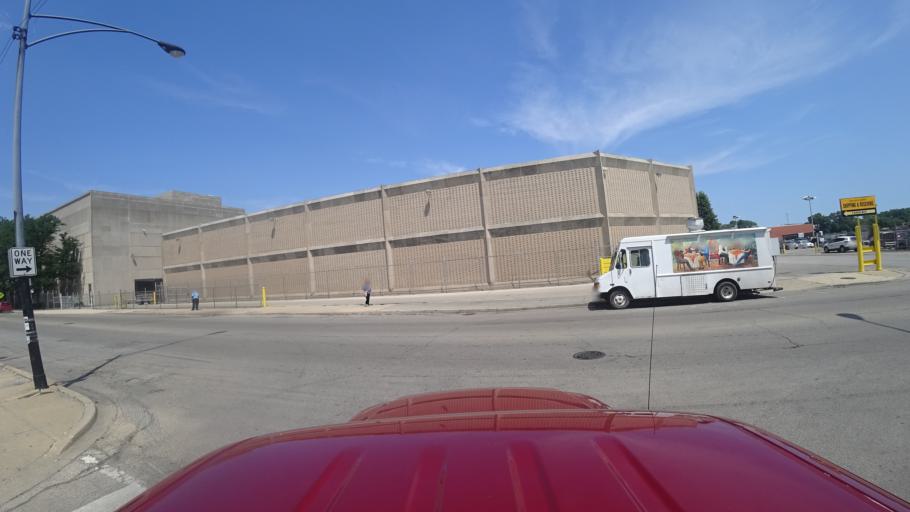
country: US
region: Illinois
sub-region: Cook County
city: Chicago
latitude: 41.8008
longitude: -87.6965
